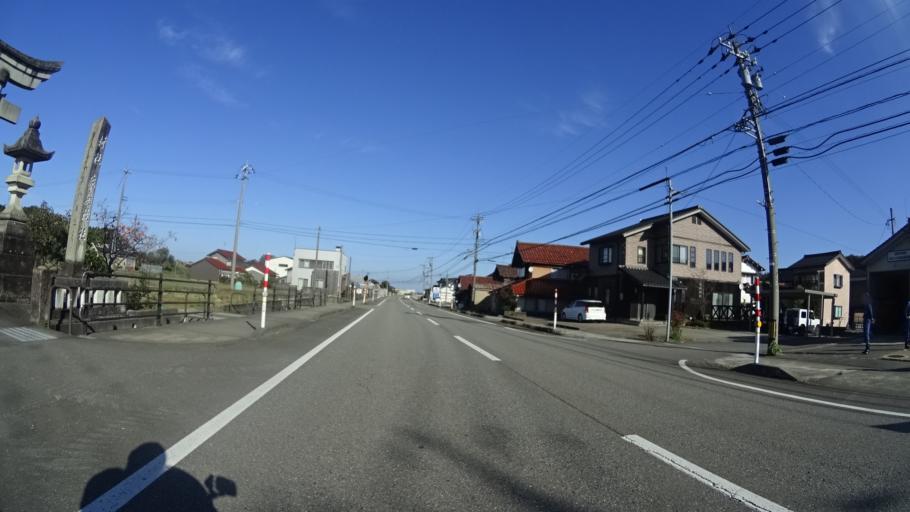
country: JP
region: Ishikawa
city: Komatsu
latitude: 36.2851
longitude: 136.3906
